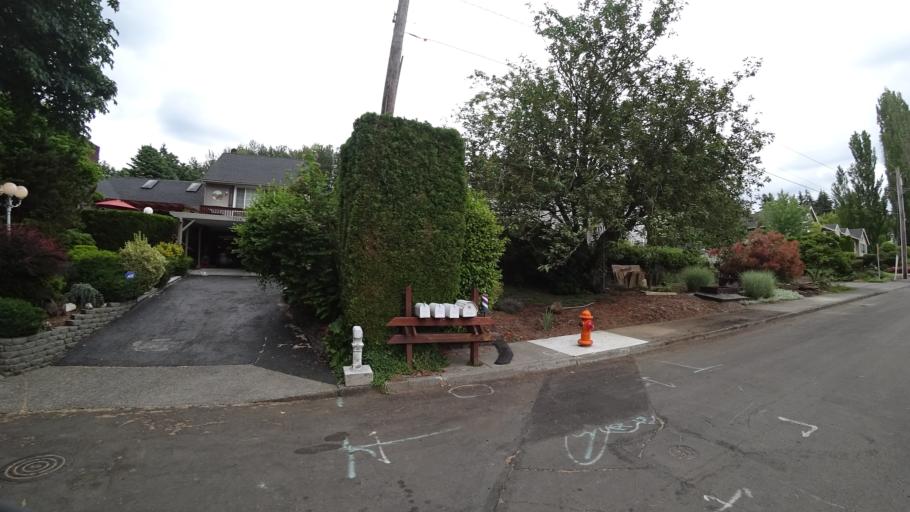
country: US
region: Oregon
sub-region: Multnomah County
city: Lents
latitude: 45.4681
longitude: -122.5628
